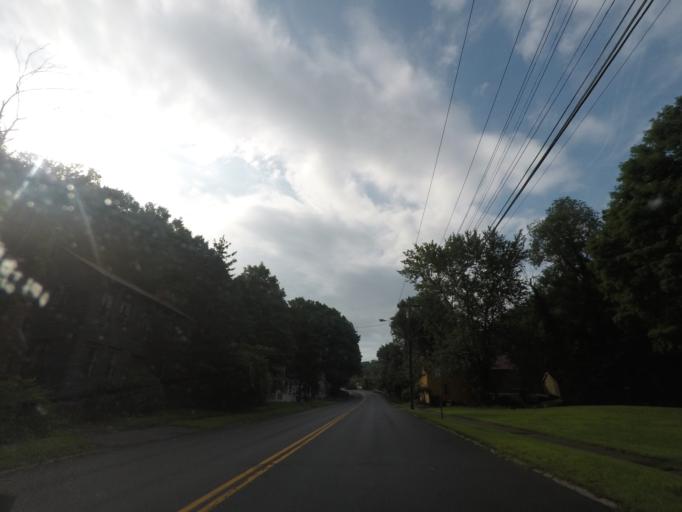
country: US
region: New York
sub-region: Rensselaer County
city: Nassau
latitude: 42.5143
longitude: -73.6061
